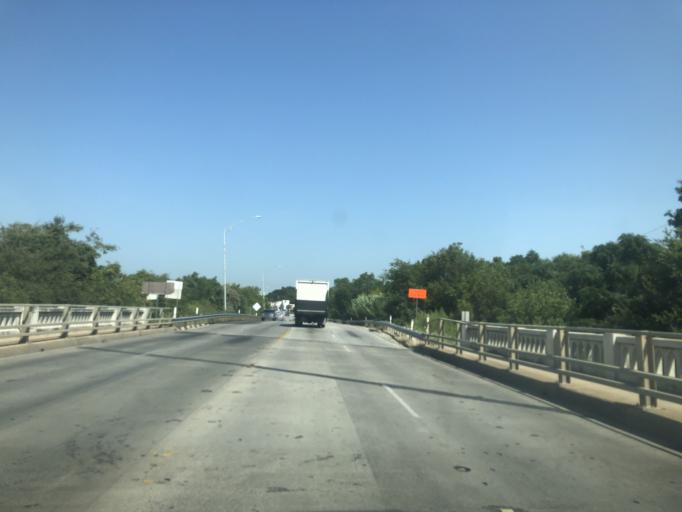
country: US
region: Texas
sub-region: Tarrant County
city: River Oaks
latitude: 32.7653
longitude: -97.3514
